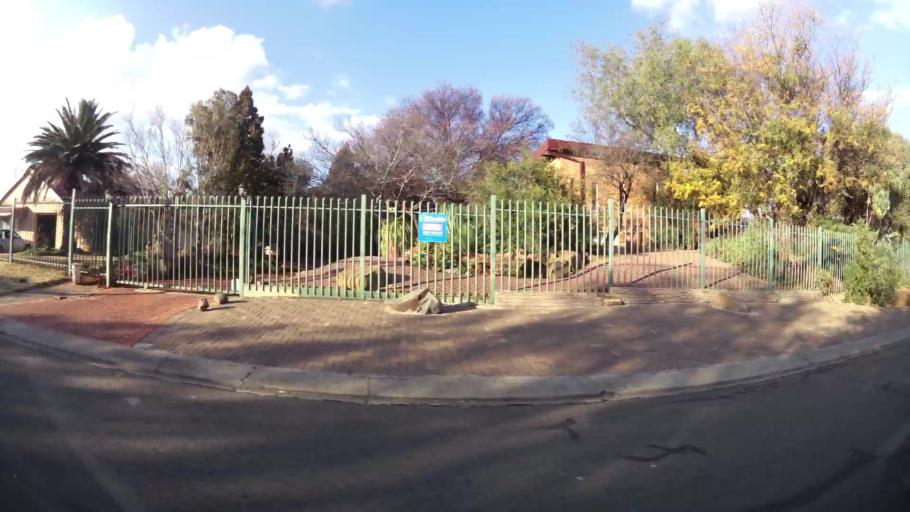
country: ZA
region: Orange Free State
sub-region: Mangaung Metropolitan Municipality
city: Bloemfontein
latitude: -29.1530
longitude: 26.1758
